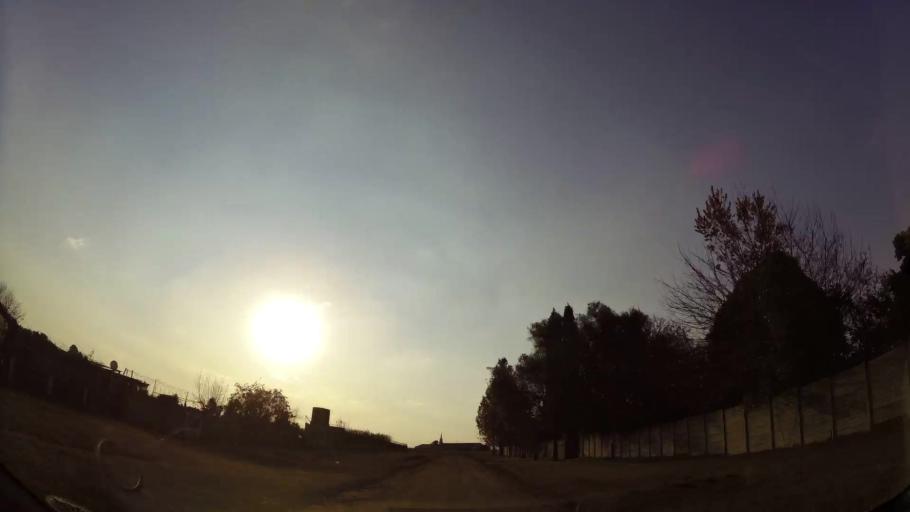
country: ZA
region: Gauteng
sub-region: Ekurhuleni Metropolitan Municipality
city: Benoni
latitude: -26.1540
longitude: 28.3677
